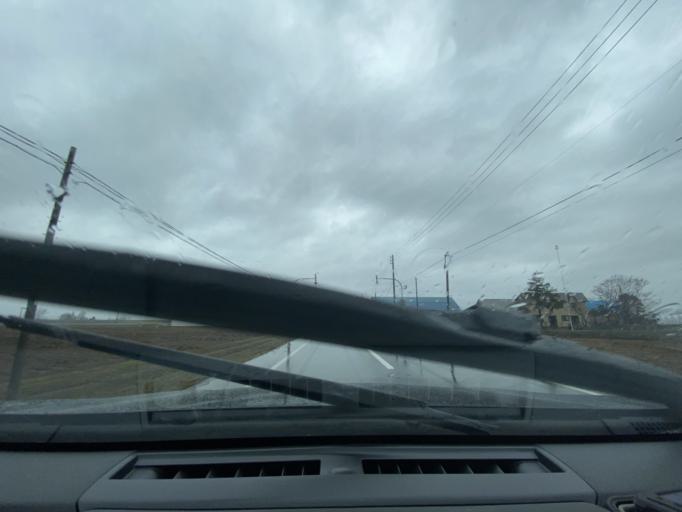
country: JP
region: Hokkaido
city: Fukagawa
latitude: 43.8099
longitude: 142.0114
